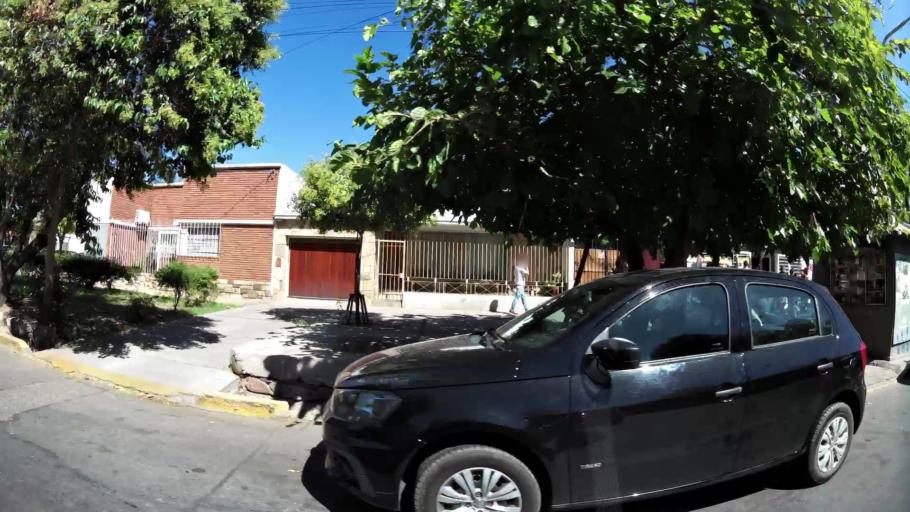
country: AR
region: Mendoza
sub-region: Departamento de Godoy Cruz
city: Godoy Cruz
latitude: -32.9149
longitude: -68.8597
